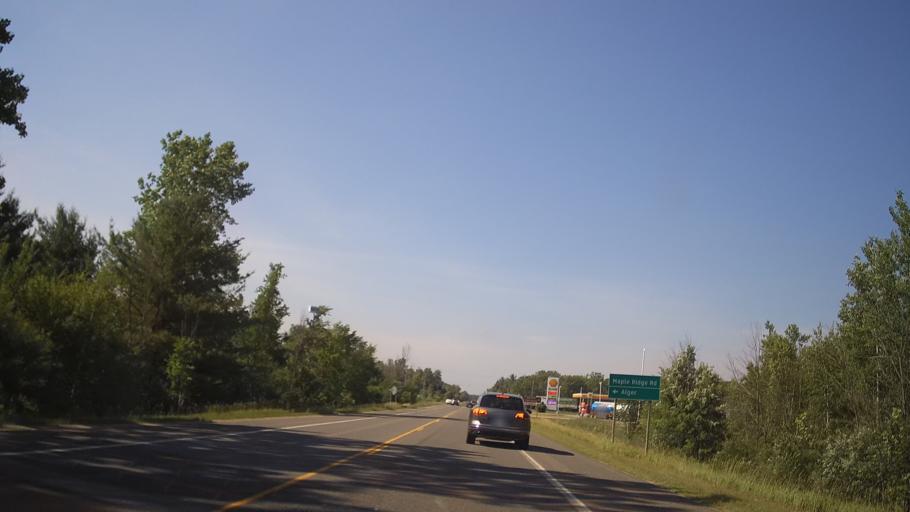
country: US
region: Michigan
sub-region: Ogemaw County
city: Skidway Lake
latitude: 44.1391
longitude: -84.1273
